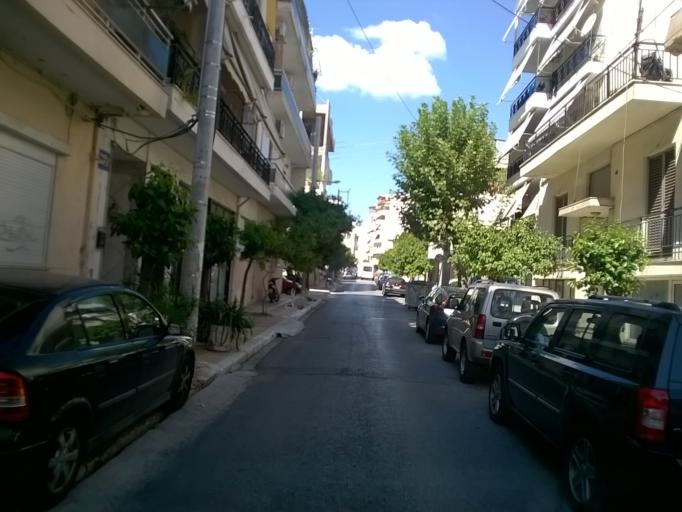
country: GR
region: Attica
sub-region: Nomos Piraios
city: Nikaia
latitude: 37.9638
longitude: 23.6529
